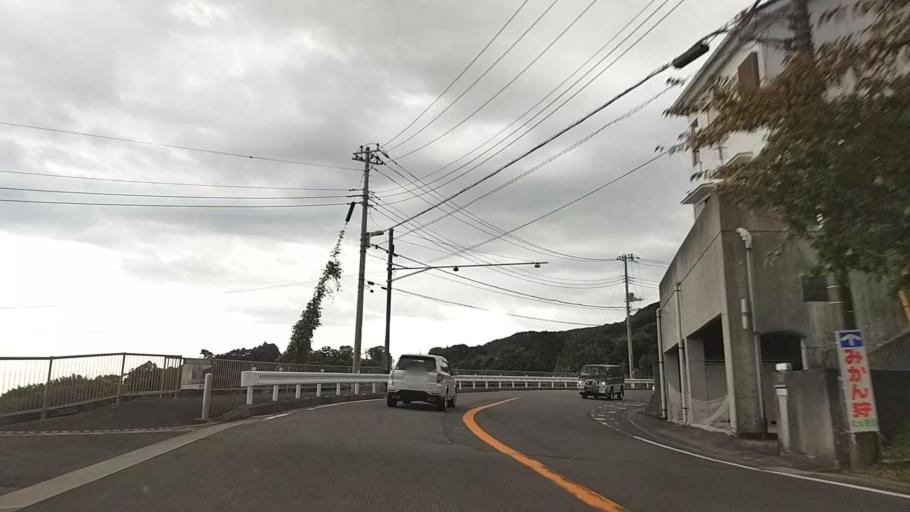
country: JP
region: Kanagawa
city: Odawara
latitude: 35.1932
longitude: 139.1338
